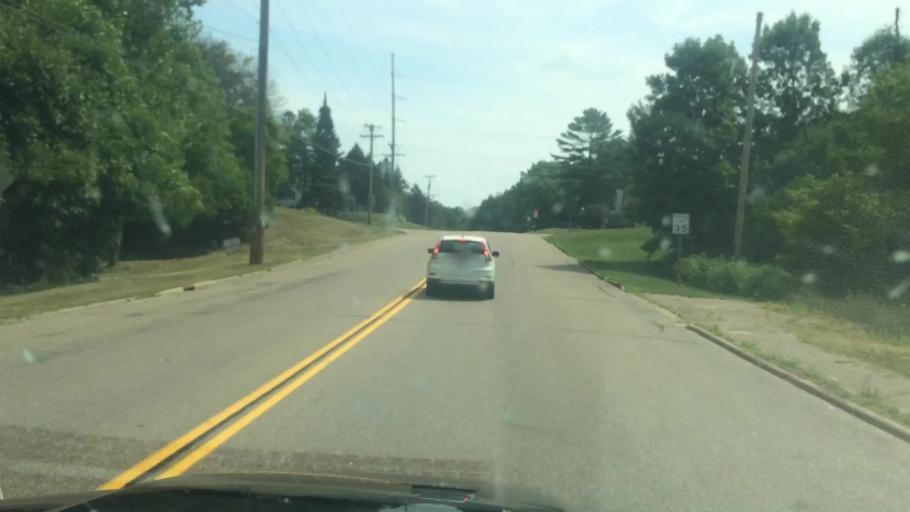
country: US
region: Wisconsin
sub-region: Langlade County
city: Antigo
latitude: 45.1684
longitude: -88.9915
